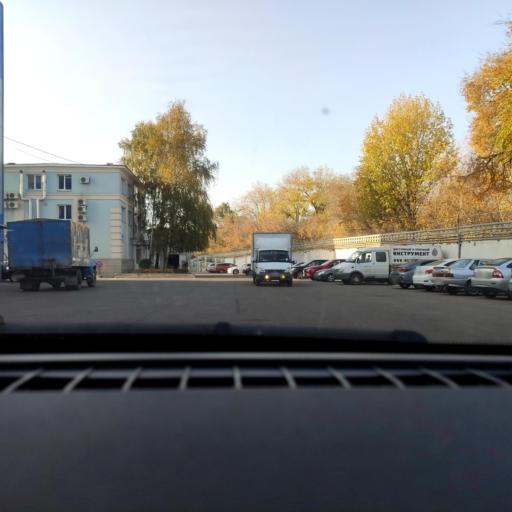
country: RU
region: Voronezj
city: Voronezh
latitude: 51.6554
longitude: 39.2806
